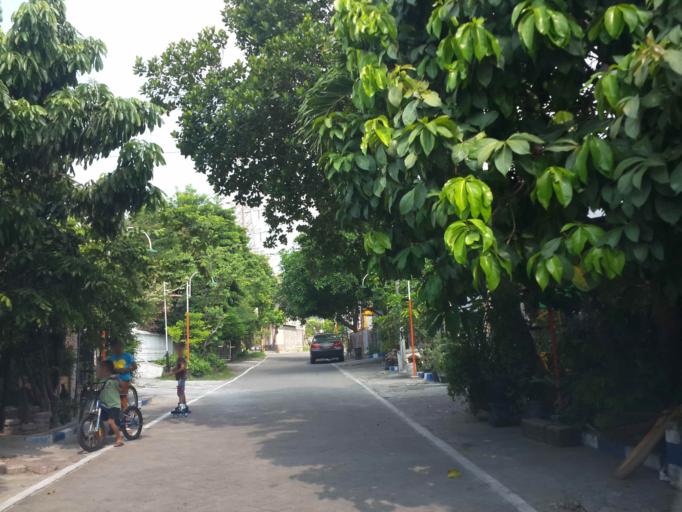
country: ID
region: East Java
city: Gresik
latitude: -7.1678
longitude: 112.6593
